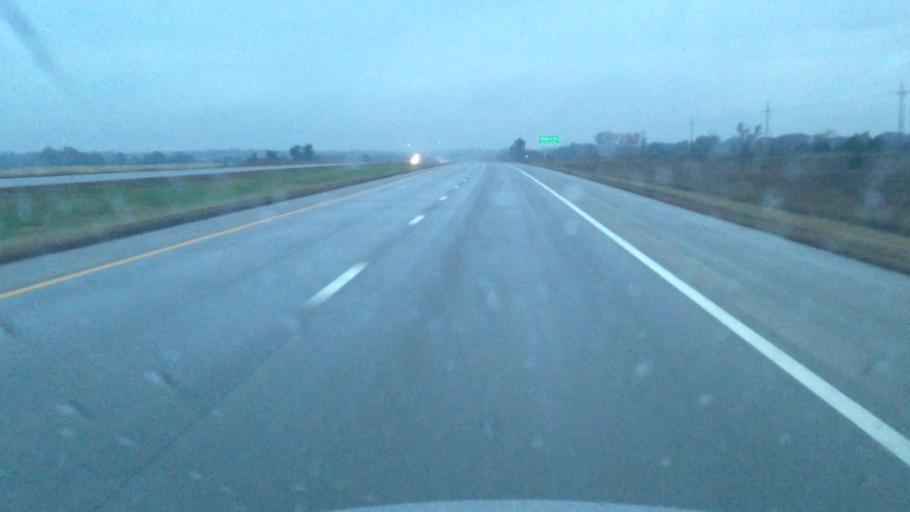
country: US
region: Kansas
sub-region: Douglas County
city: Baldwin City
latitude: 38.7326
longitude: -95.2685
